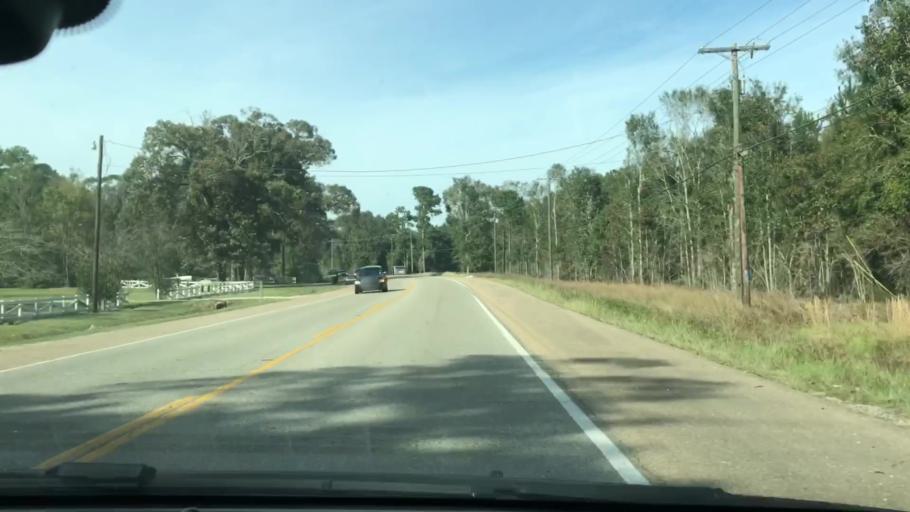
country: US
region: Louisiana
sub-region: Saint Tammany Parish
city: Pearl River
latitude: 30.4017
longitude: -89.7644
